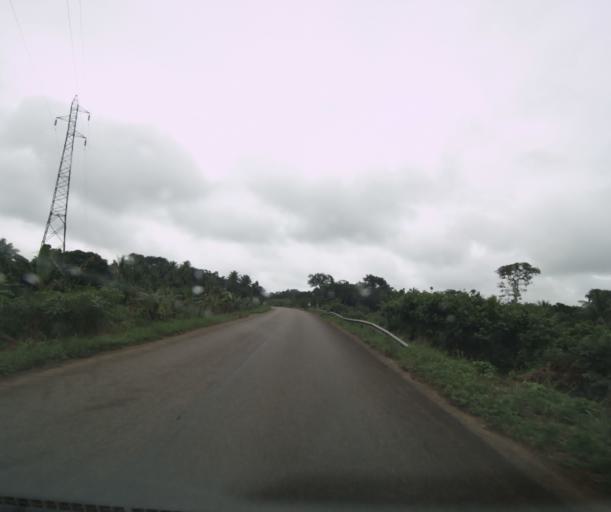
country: CM
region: Littoral
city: Edea
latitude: 3.6980
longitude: 10.1045
